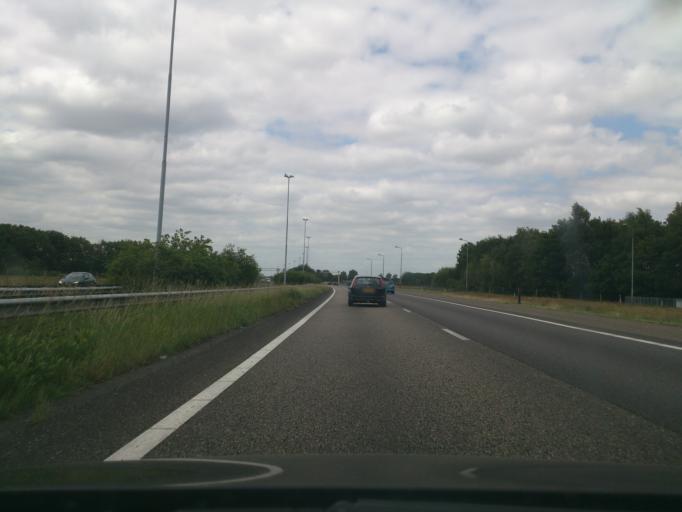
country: NL
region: North Brabant
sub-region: Gemeente Dongen
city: Dongen
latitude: 51.5588
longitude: 4.8865
